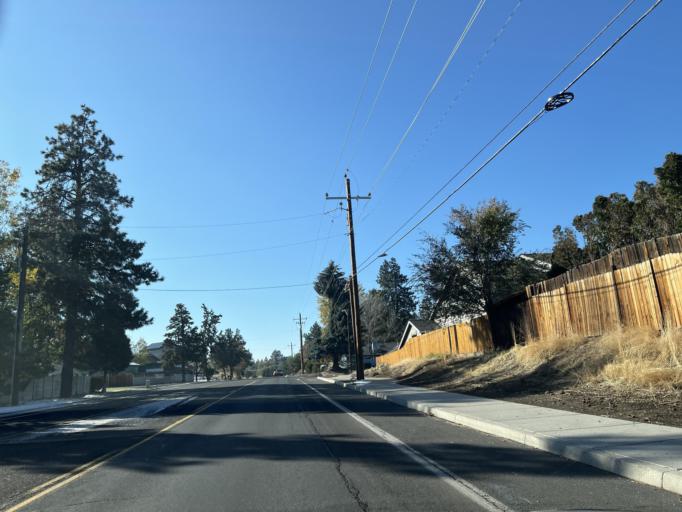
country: US
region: Oregon
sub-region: Deschutes County
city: Bend
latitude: 44.0781
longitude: -121.2851
